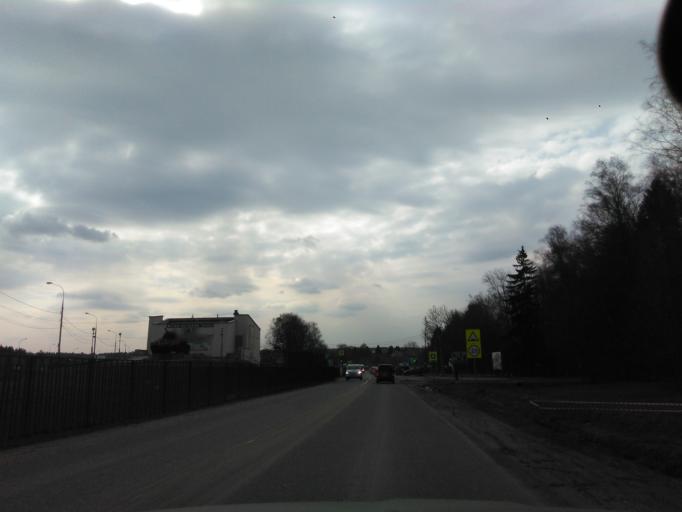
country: RU
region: Moskovskaya
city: Marfino
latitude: 56.0557
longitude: 37.5284
